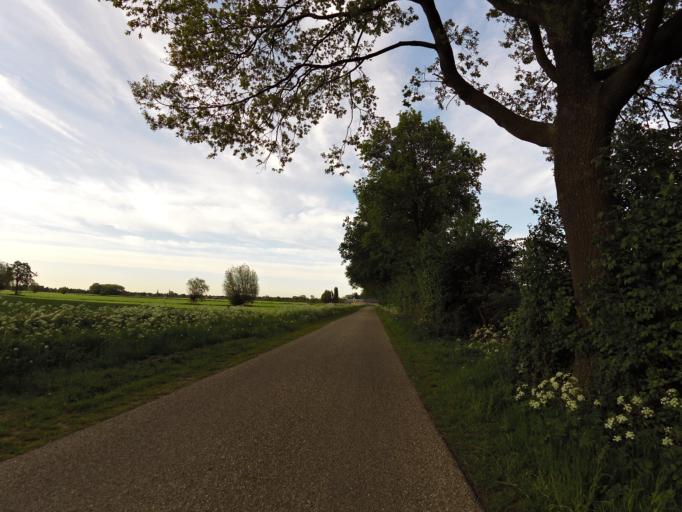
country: NL
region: Gelderland
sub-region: Oude IJsselstreek
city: Gendringen
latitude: 51.8558
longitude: 6.3700
